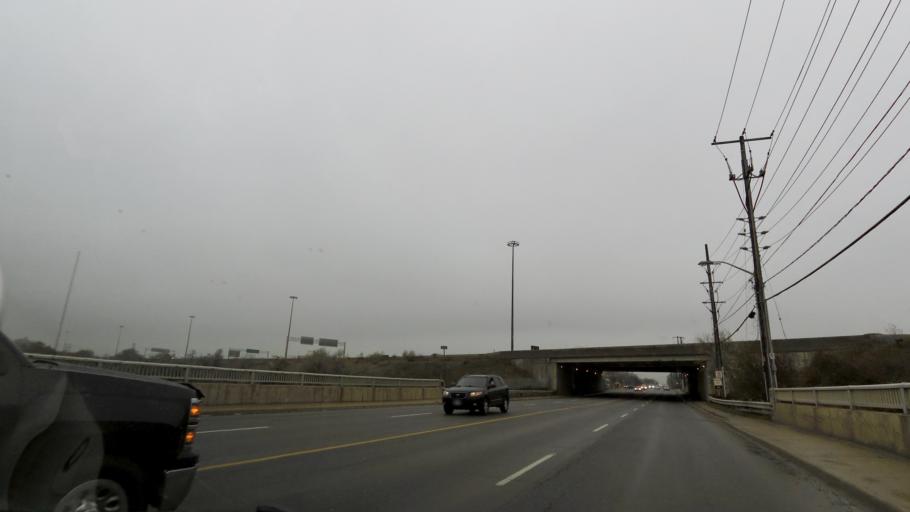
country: CA
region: Ontario
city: Etobicoke
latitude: 43.6977
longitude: -79.6006
